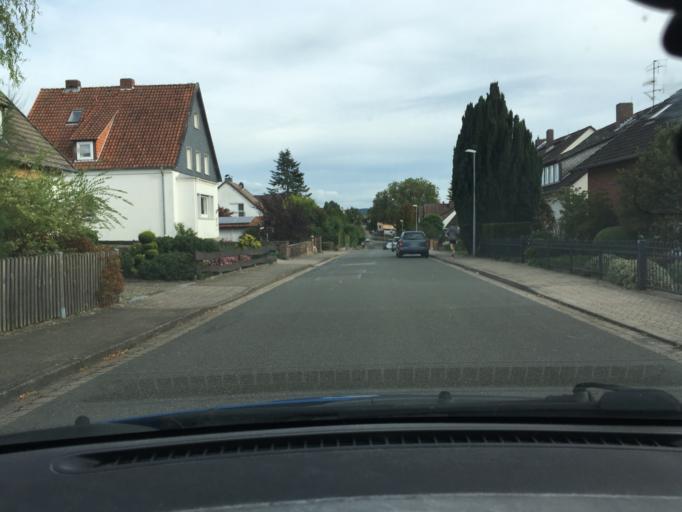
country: DE
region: Lower Saxony
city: Bad Munder am Deister
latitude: 52.2022
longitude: 9.4654
